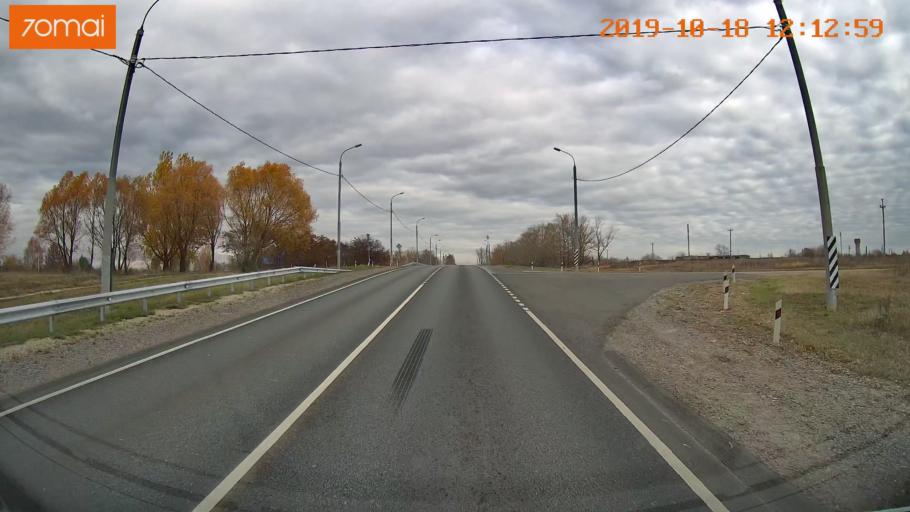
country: RU
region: Rjazan
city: Zakharovo
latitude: 54.4173
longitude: 39.3651
